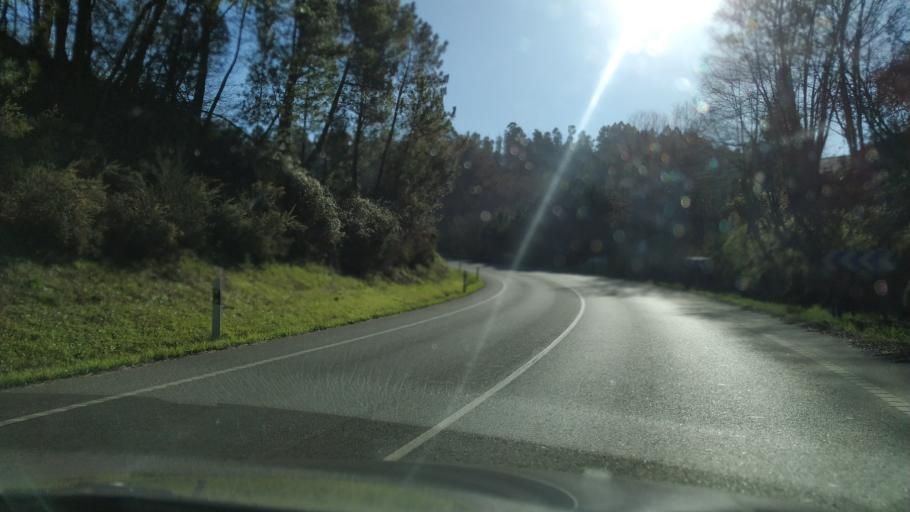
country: ES
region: Galicia
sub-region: Provincia de Pontevedra
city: Silleda
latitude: 42.7304
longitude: -8.3183
